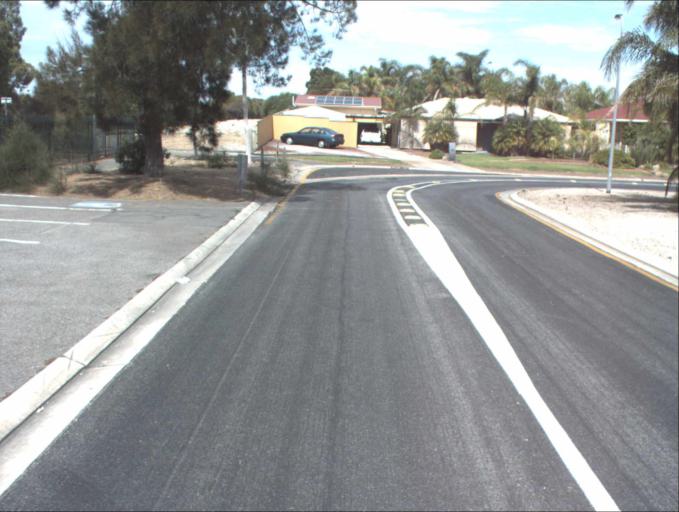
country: AU
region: South Australia
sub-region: Port Adelaide Enfield
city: Birkenhead
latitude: -34.7865
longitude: 138.4948
